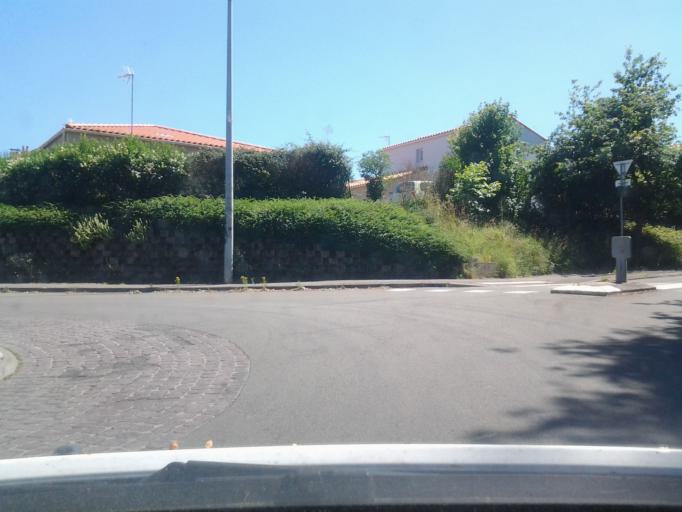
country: FR
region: Pays de la Loire
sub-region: Departement de la Vendee
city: La Roche-sur-Yon
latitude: 46.6649
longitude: -1.4150
